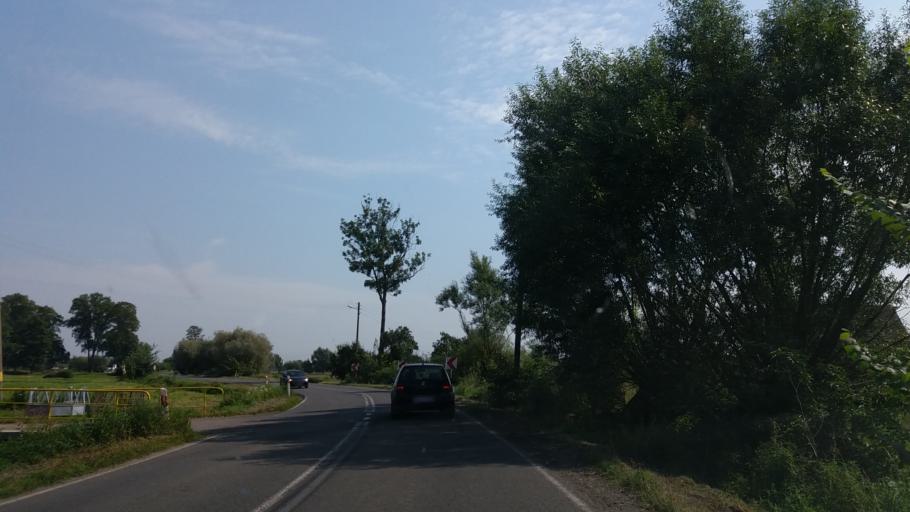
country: PL
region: Lubusz
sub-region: Powiat strzelecko-drezdenecki
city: Zwierzyn
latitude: 52.8220
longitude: 15.6162
